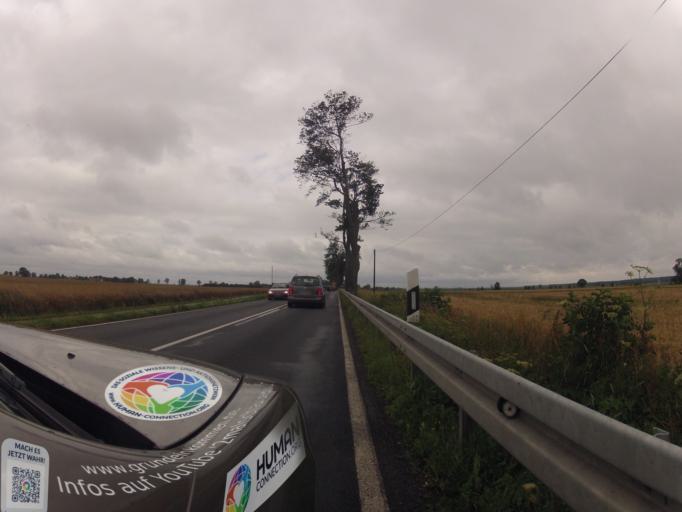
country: DE
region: Mecklenburg-Vorpommern
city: Usedom
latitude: 53.8690
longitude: 13.8474
